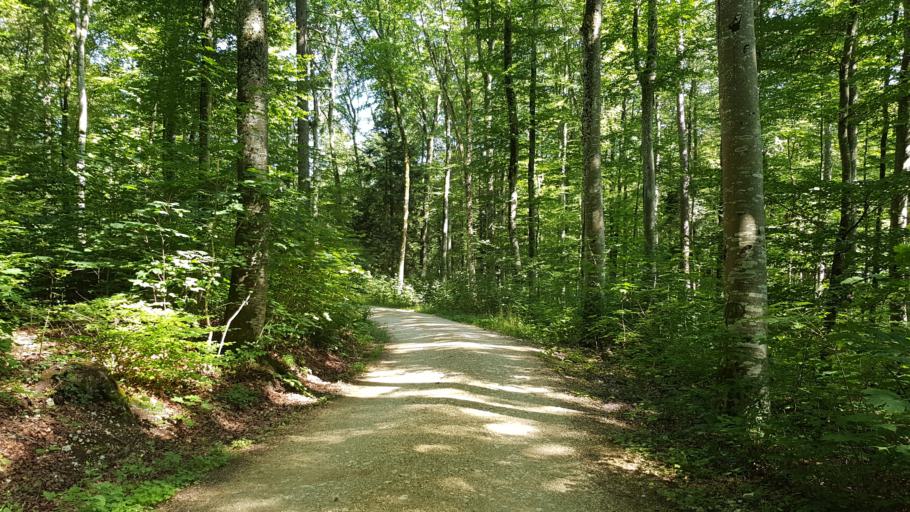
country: CH
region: Schaffhausen
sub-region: Bezirk Schaffhausen
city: Beringen
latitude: 47.7456
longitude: 8.5794
